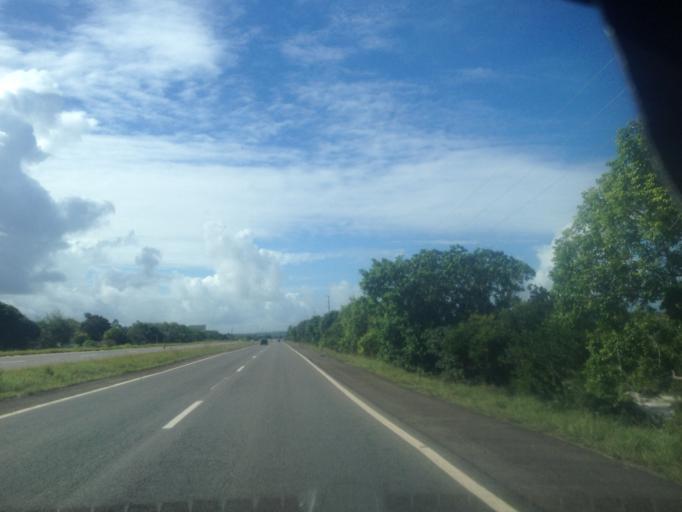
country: BR
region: Bahia
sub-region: Mata De Sao Joao
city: Mata de Sao Joao
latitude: -12.6256
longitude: -38.0618
